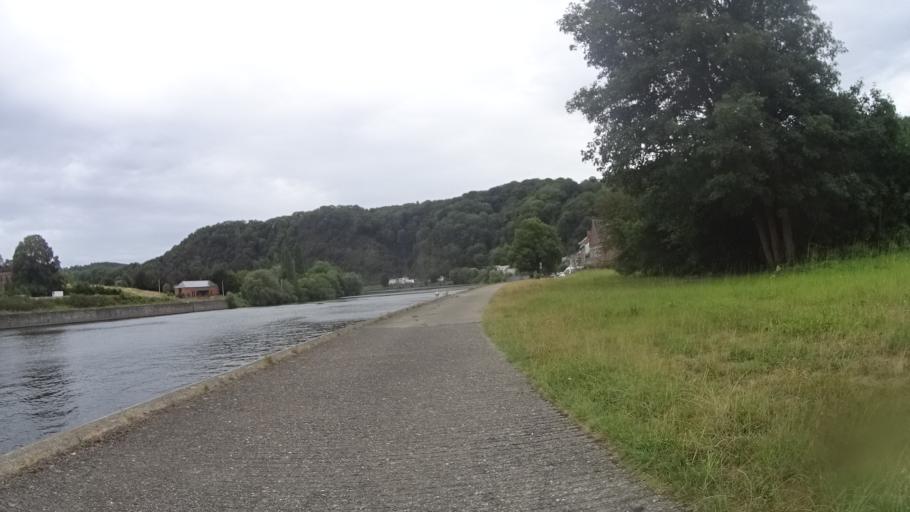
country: BE
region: Wallonia
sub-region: Province de Liege
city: Huy
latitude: 50.5216
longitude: 5.2233
